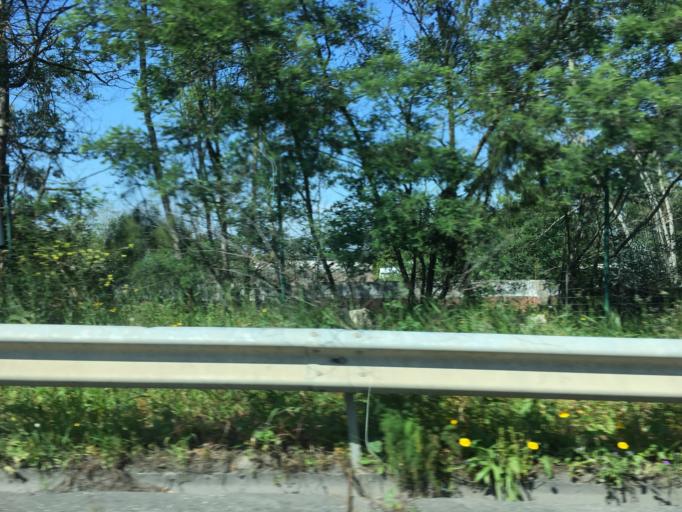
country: PT
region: Lisbon
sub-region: Sintra
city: Belas
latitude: 38.7886
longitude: -9.2369
